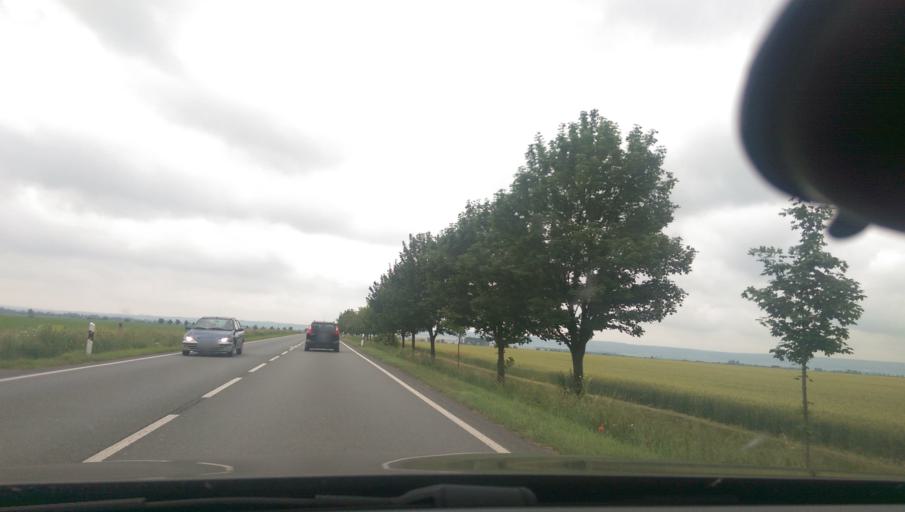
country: DE
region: Thuringia
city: Gebesee
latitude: 51.1070
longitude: 10.9301
